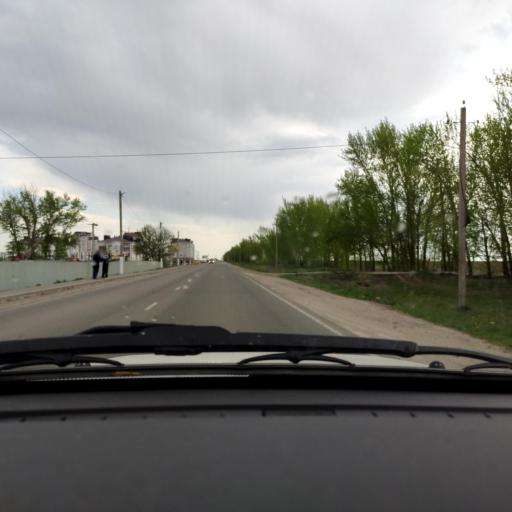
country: RU
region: Voronezj
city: Novaya Usman'
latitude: 51.6059
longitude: 39.3733
